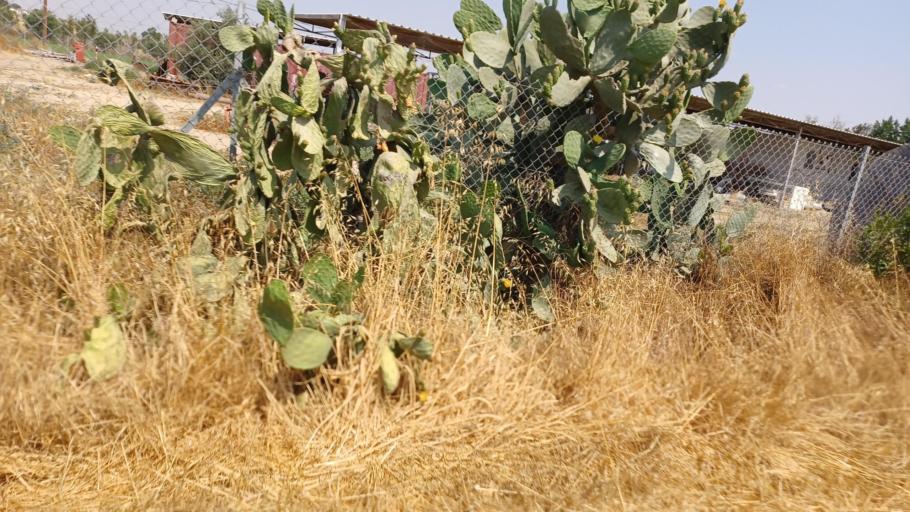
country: CY
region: Lefkosia
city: Dali
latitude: 35.0441
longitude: 33.4417
